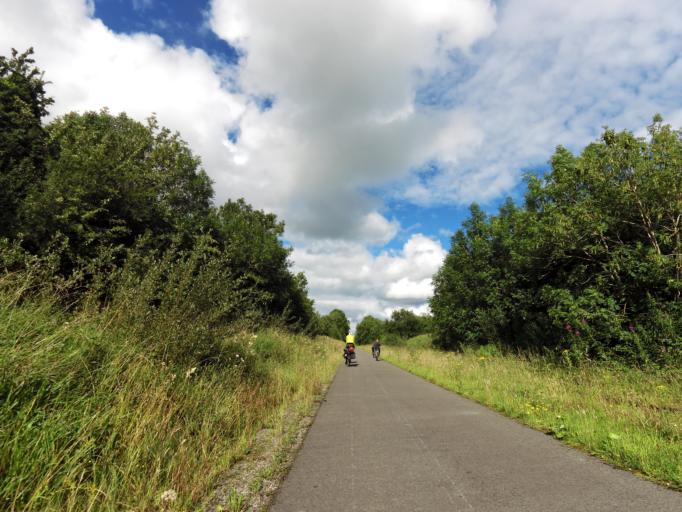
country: IE
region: Leinster
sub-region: An Iarmhi
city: Kilbeggan
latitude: 53.4435
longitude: -7.5470
